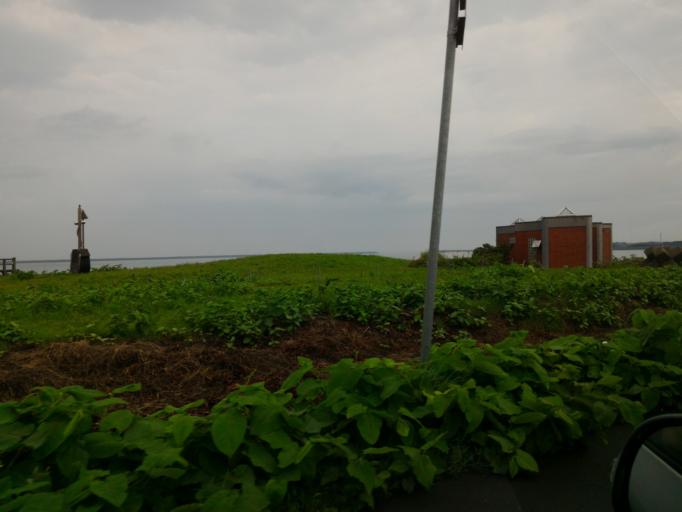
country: JP
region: Hokkaido
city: Rumoi
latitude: 43.9625
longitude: 141.6431
